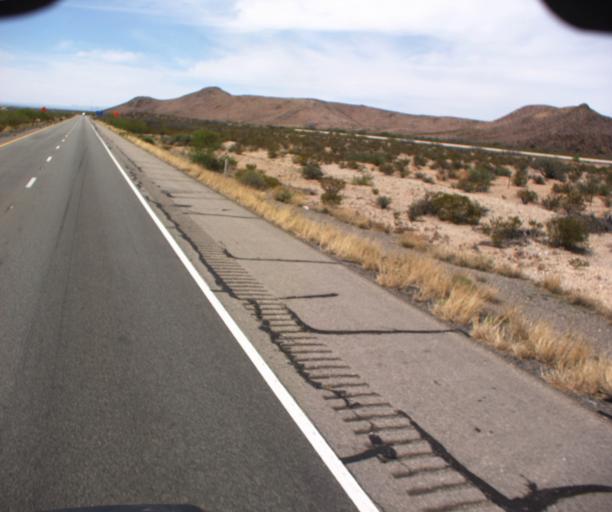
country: US
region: New Mexico
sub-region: Hidalgo County
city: Lordsburg
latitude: 32.2345
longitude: -109.0722
